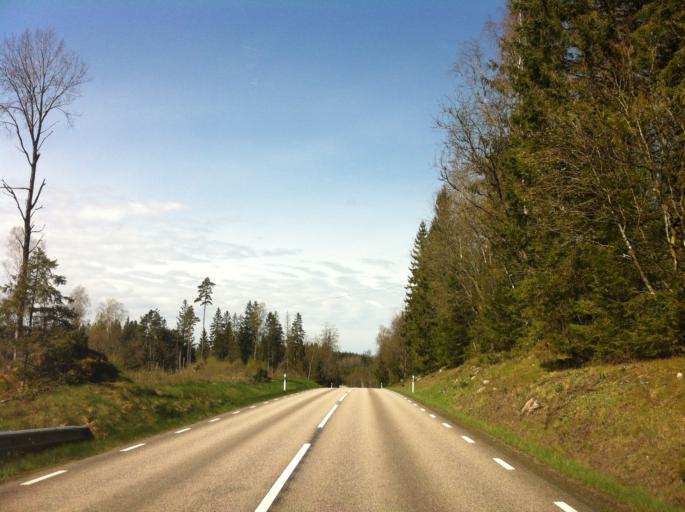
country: SE
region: Vaestra Goetaland
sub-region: Marks Kommun
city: Kinna
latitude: 57.2056
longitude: 12.8285
